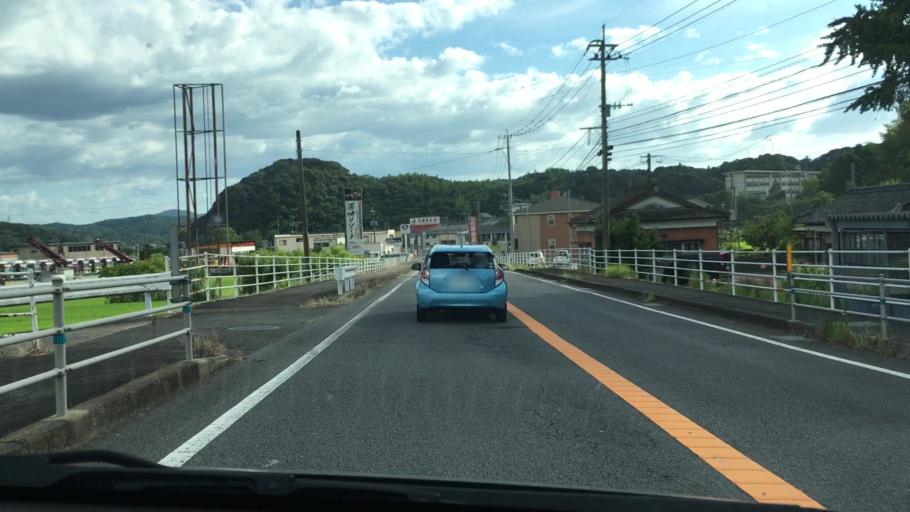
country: JP
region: Nagasaki
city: Sasebo
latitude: 33.1611
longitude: 129.8327
